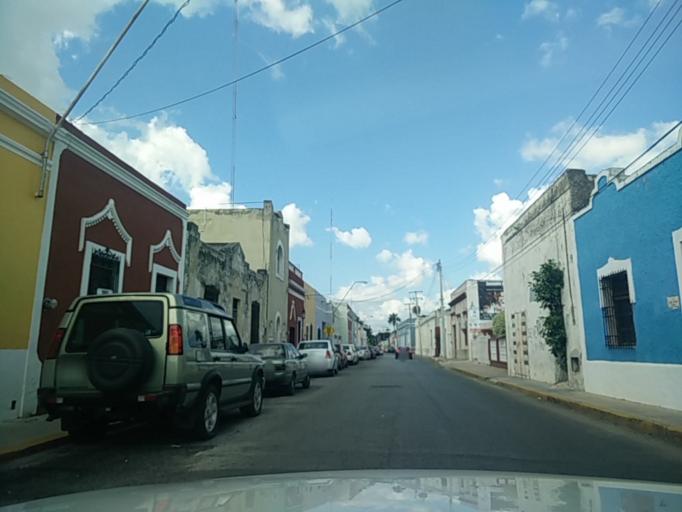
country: MX
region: Yucatan
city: Merida
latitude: 20.9817
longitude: -89.6193
